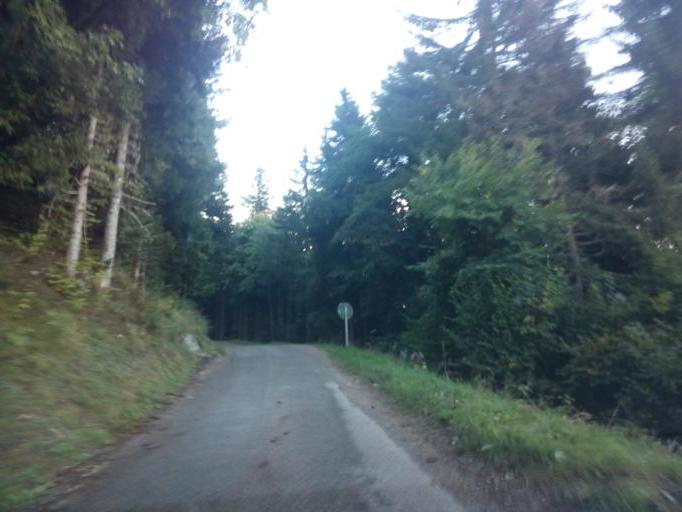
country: FR
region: Rhone-Alpes
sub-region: Departement de l'Isere
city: Le Champ-pres-Froges
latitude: 45.2364
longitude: 5.9850
